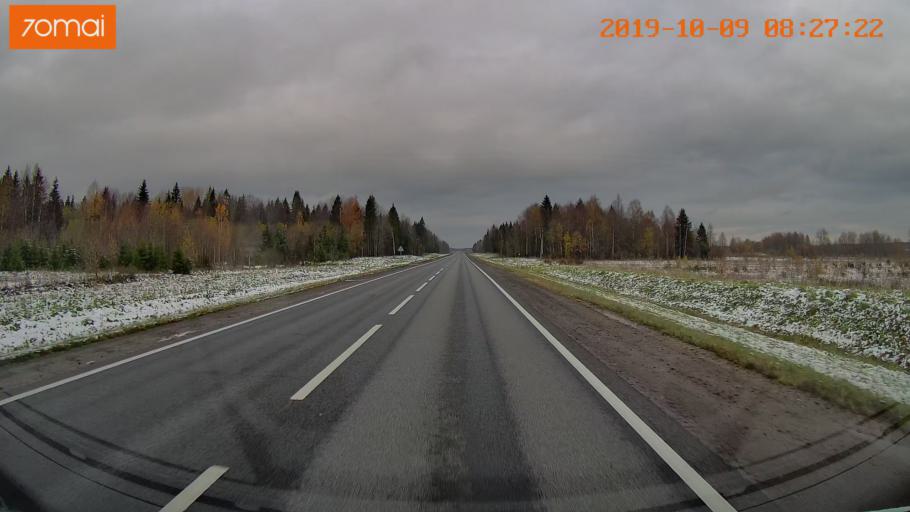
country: RU
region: Vologda
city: Gryazovets
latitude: 58.8029
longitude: 40.2497
